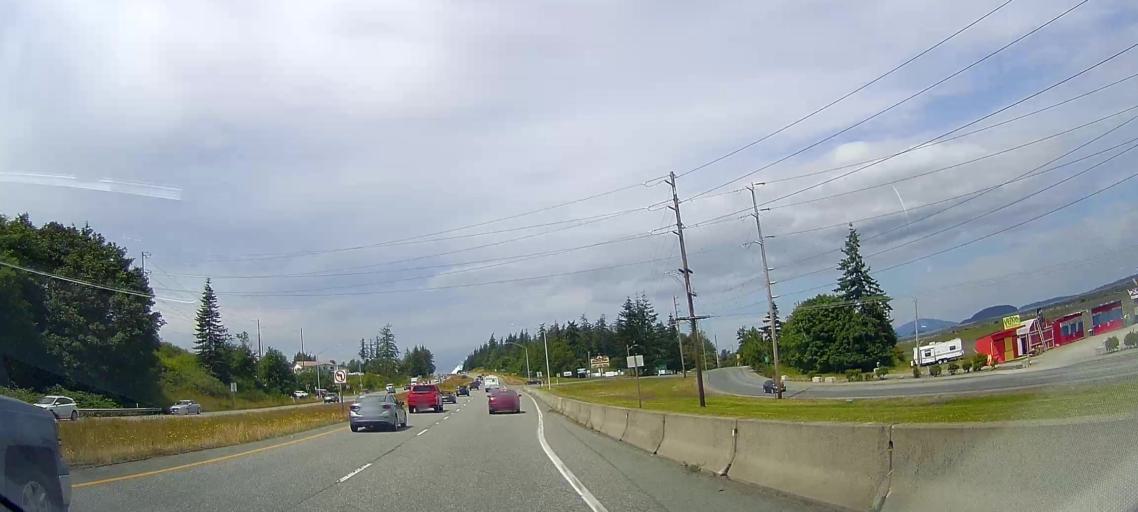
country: US
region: Washington
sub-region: Skagit County
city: Anacortes
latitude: 48.4579
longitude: -122.5240
